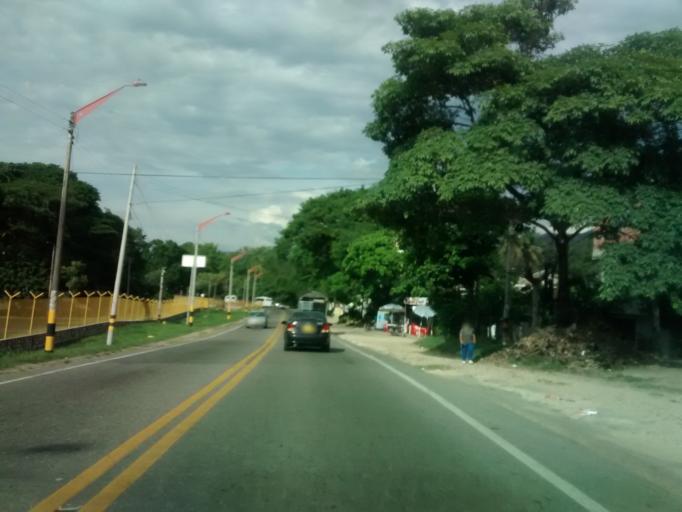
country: CO
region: Tolima
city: Melgar
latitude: 4.2162
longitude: -74.6281
